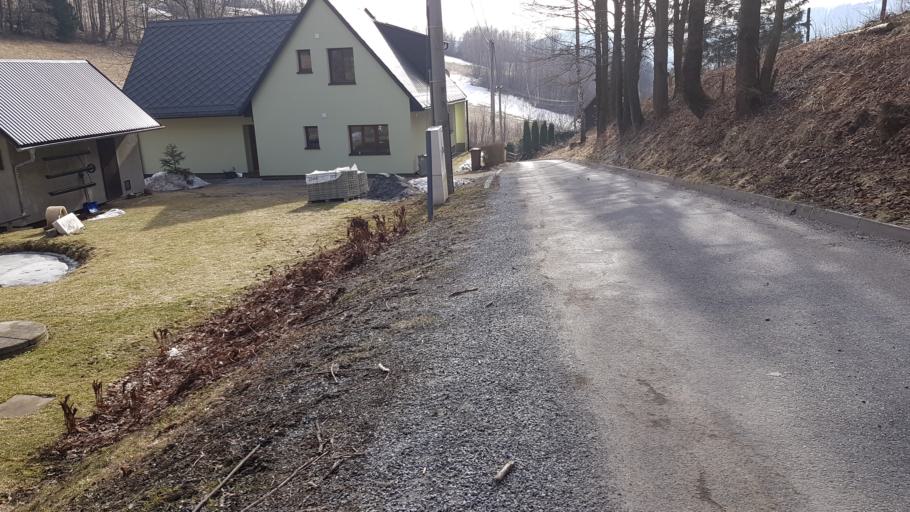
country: CZ
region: Olomoucky
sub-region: Okres Jesenik
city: Jesenik
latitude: 50.2247
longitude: 17.2276
